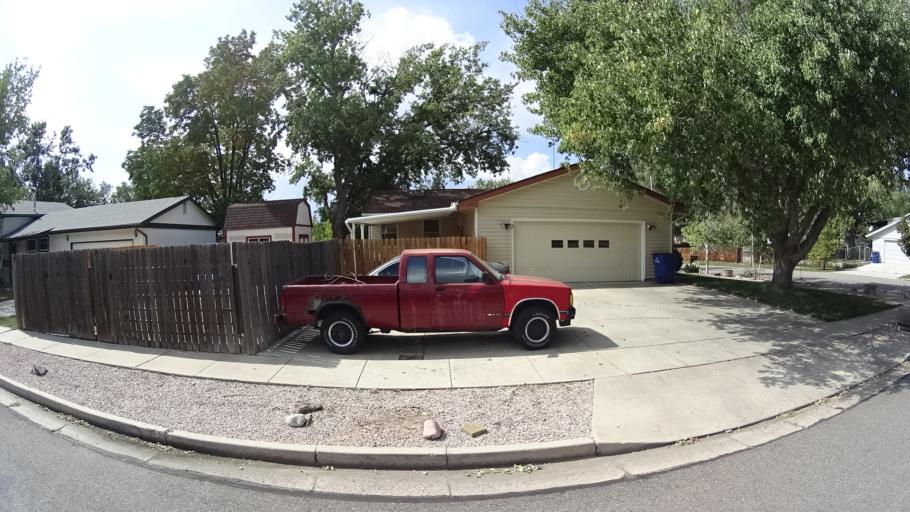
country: US
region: Colorado
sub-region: El Paso County
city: Cimarron Hills
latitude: 38.8527
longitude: -104.7415
